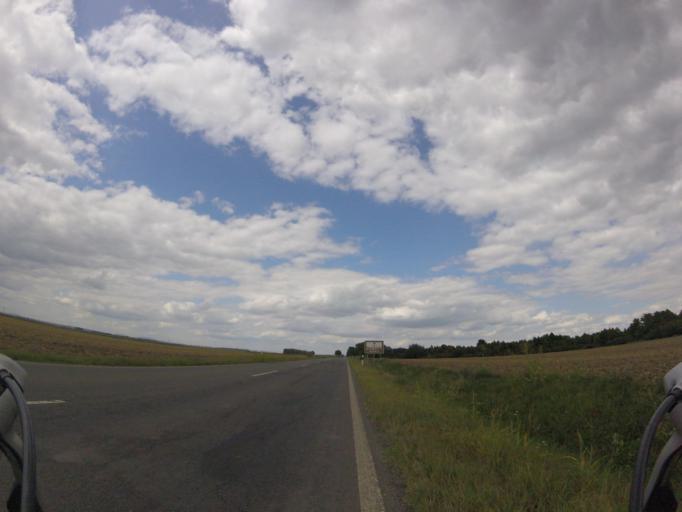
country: HU
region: Baranya
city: Mohacs
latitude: 45.9188
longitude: 18.6595
